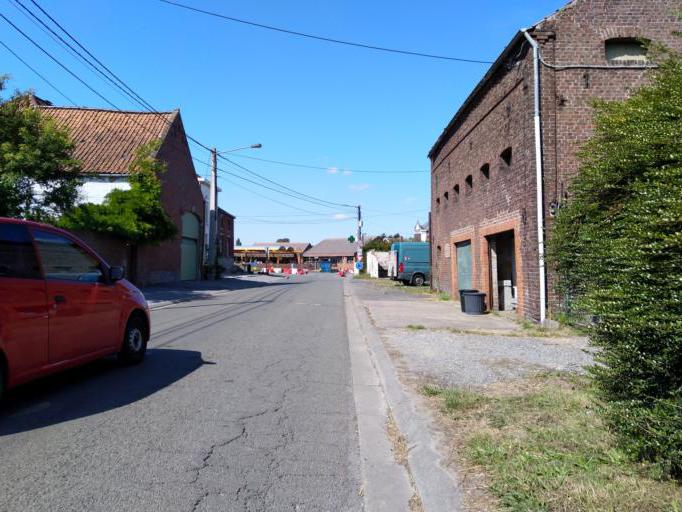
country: BE
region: Wallonia
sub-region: Province du Hainaut
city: Jurbise
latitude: 50.5261
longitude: 3.8589
